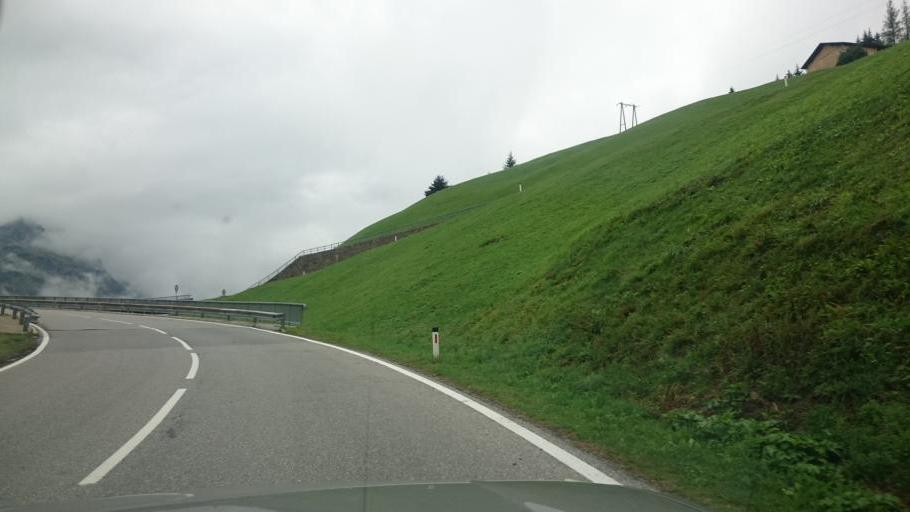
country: AT
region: Vorarlberg
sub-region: Politischer Bezirk Bregenz
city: Schroecken
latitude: 47.2606
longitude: 10.0940
